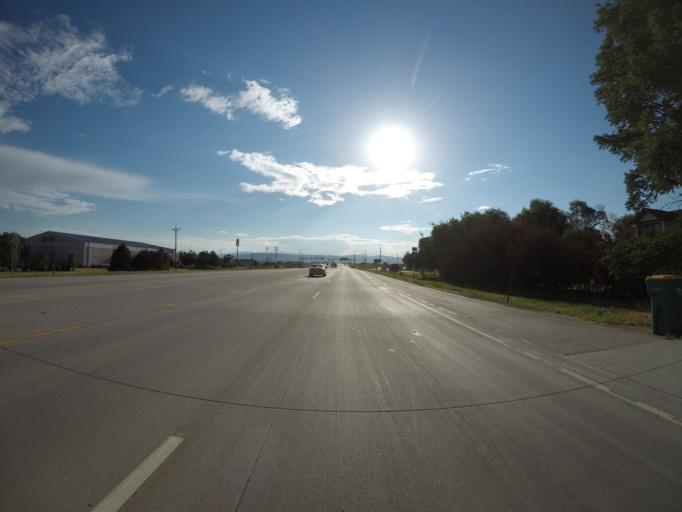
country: US
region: Colorado
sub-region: Larimer County
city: Fort Collins
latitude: 40.5812
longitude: -104.9944
